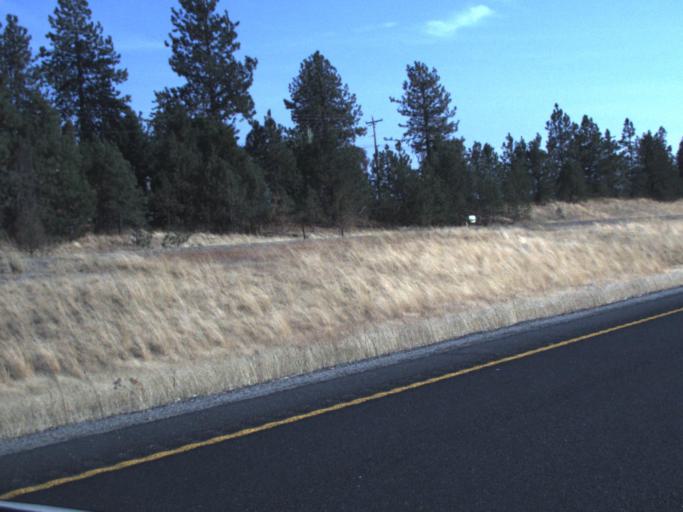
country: US
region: Washington
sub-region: Spokane County
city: Deer Park
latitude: 48.0588
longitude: -117.3448
